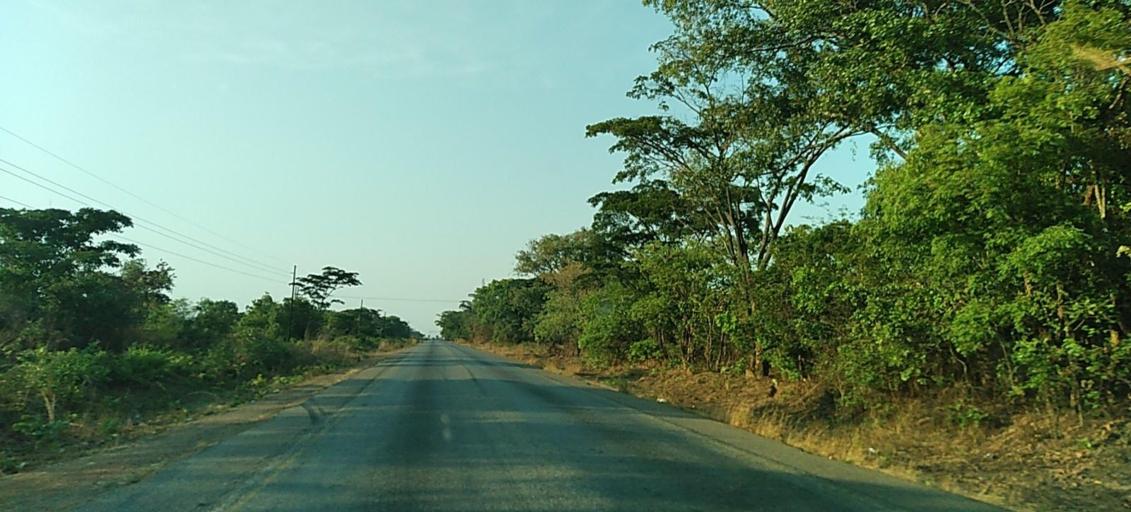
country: ZM
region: Copperbelt
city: Ndola
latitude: -13.2351
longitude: 28.6792
